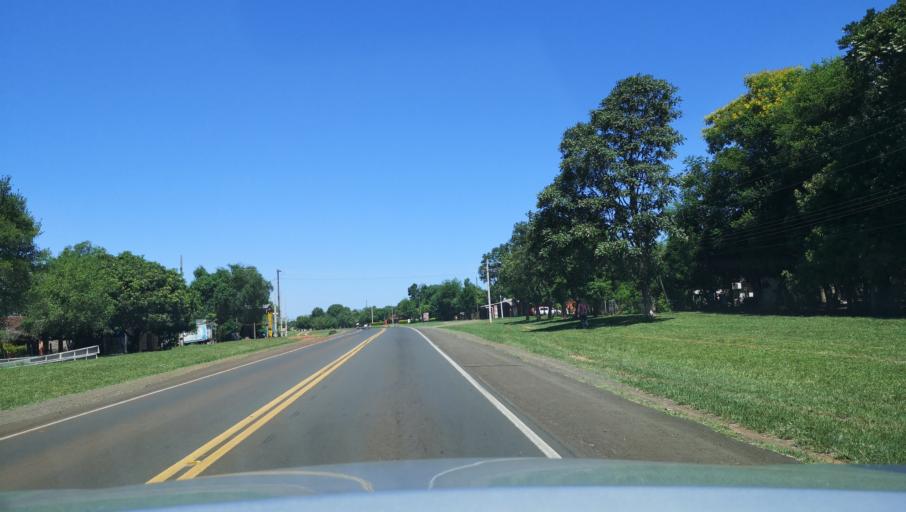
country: PY
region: Misiones
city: Santa Rosa
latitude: -26.8965
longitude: -56.9202
